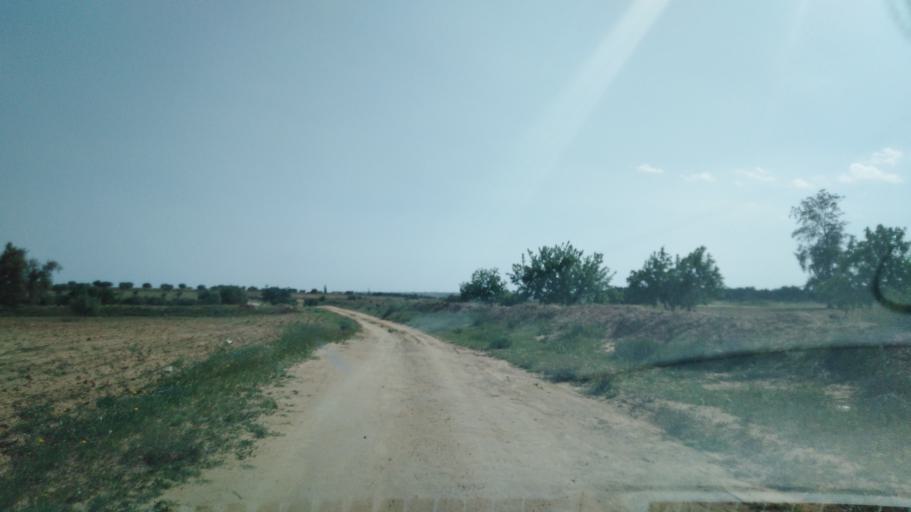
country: TN
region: Safaqis
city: Bi'r `Ali Bin Khalifah
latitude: 34.7901
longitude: 10.3707
